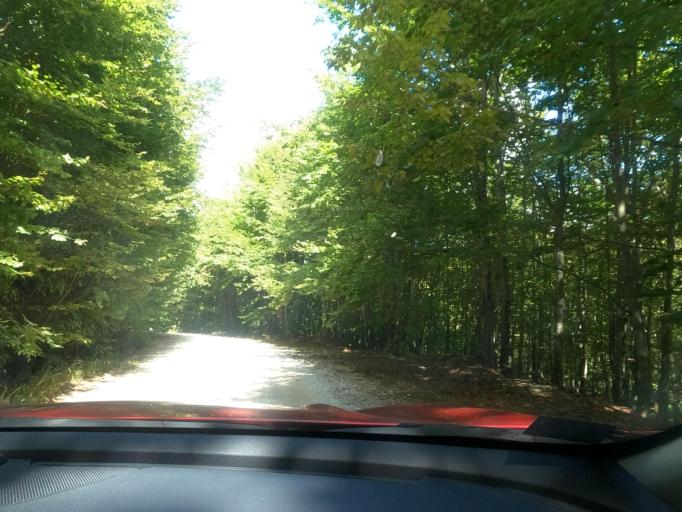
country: HR
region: Karlovacka
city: Vojnic
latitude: 45.2758
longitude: 15.7792
